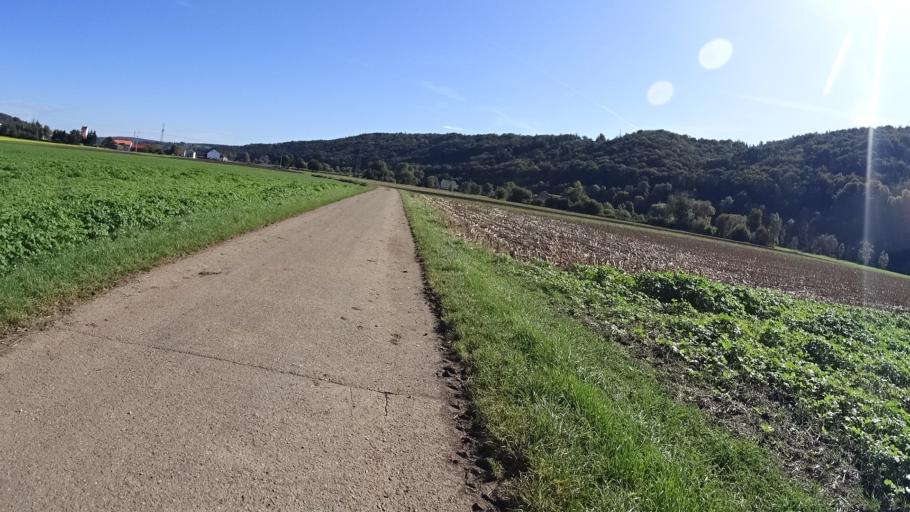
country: DE
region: Bavaria
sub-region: Upper Bavaria
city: Eichstaett
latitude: 48.8764
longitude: 11.2277
